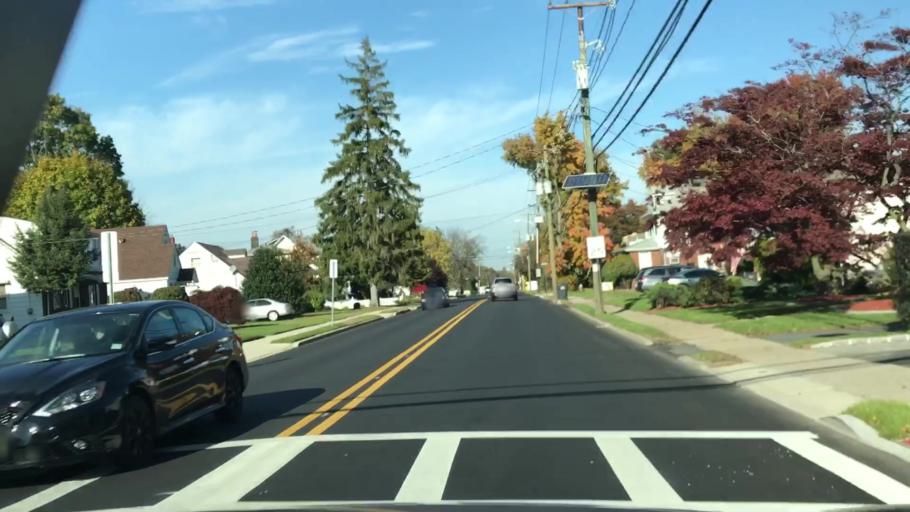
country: US
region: New Jersey
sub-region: Bergen County
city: Bergenfield
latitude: 40.9188
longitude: -74.0085
